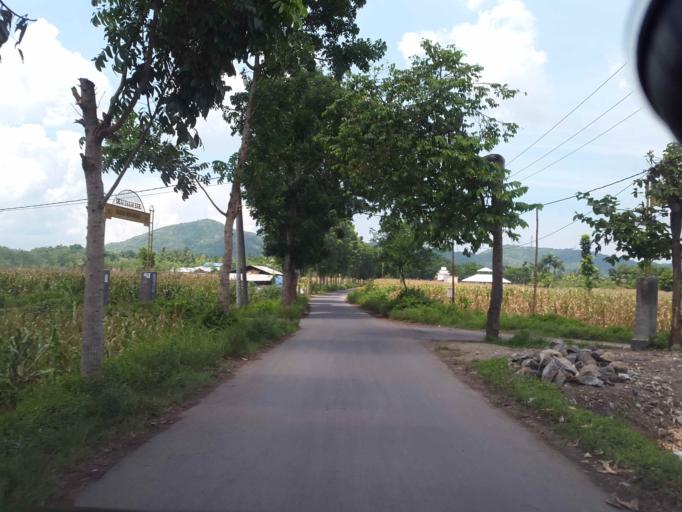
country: ID
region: West Nusa Tenggara
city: Karangkebon Timur
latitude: -8.6595
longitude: 116.1242
